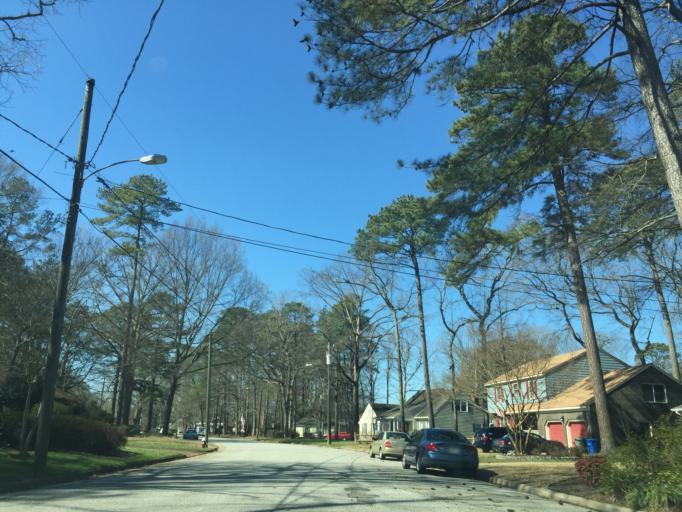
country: US
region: Virginia
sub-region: City of Newport News
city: Newport News
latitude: 37.0818
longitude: -76.4911
